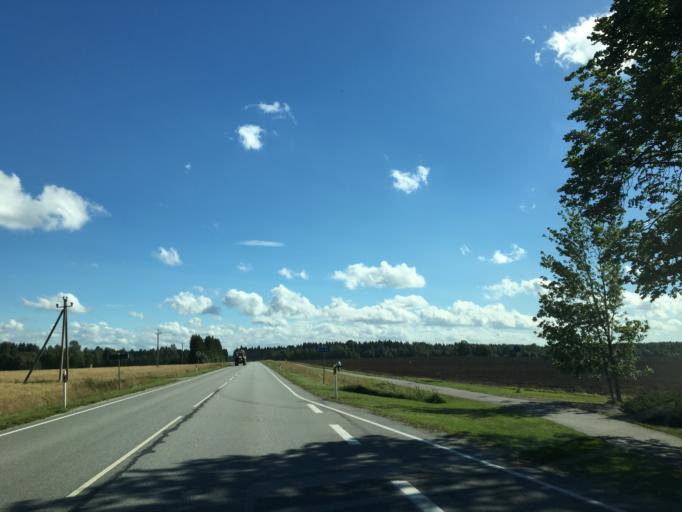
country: EE
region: Paernumaa
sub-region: Vaendra vald (alev)
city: Vandra
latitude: 58.6373
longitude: 25.0997
